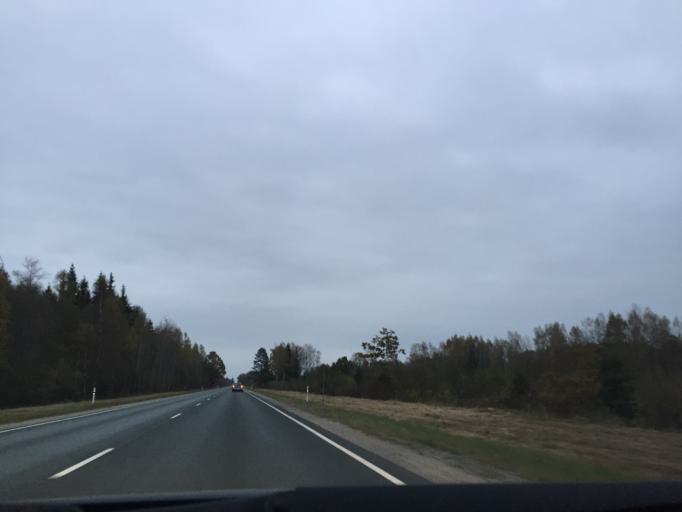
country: LV
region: Ozolnieku
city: Ozolnieki
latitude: 56.7180
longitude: 23.8397
